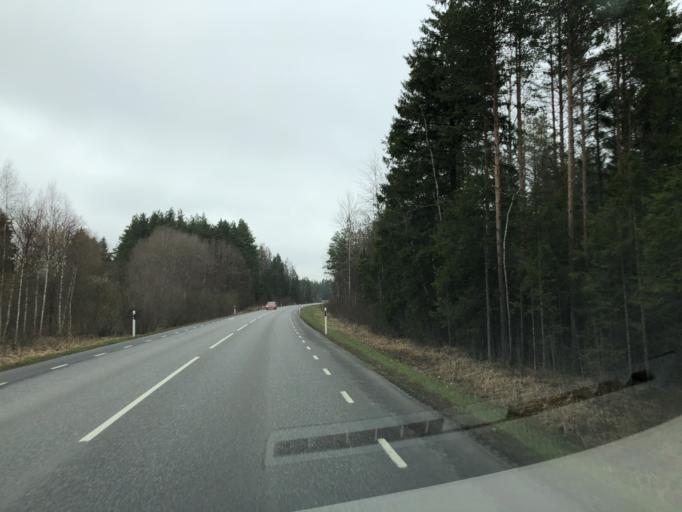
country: EE
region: Laeaene-Virumaa
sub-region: Rakke vald
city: Rakke
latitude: 59.0334
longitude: 26.2378
